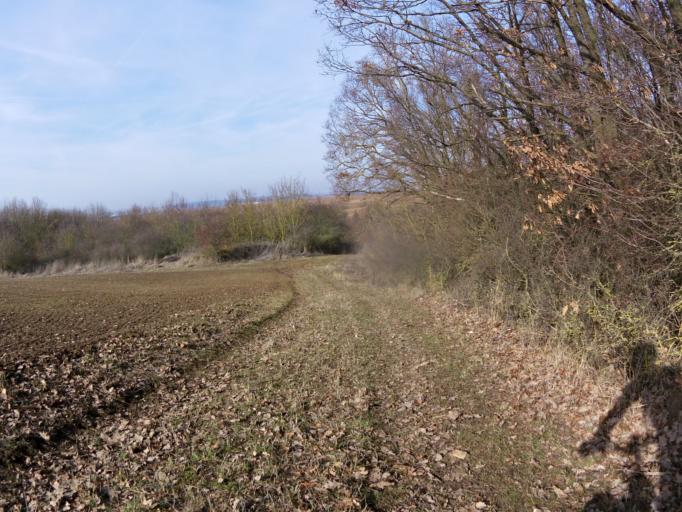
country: DE
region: Bavaria
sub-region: Regierungsbezirk Unterfranken
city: Kurnach
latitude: 49.8282
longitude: 10.0362
